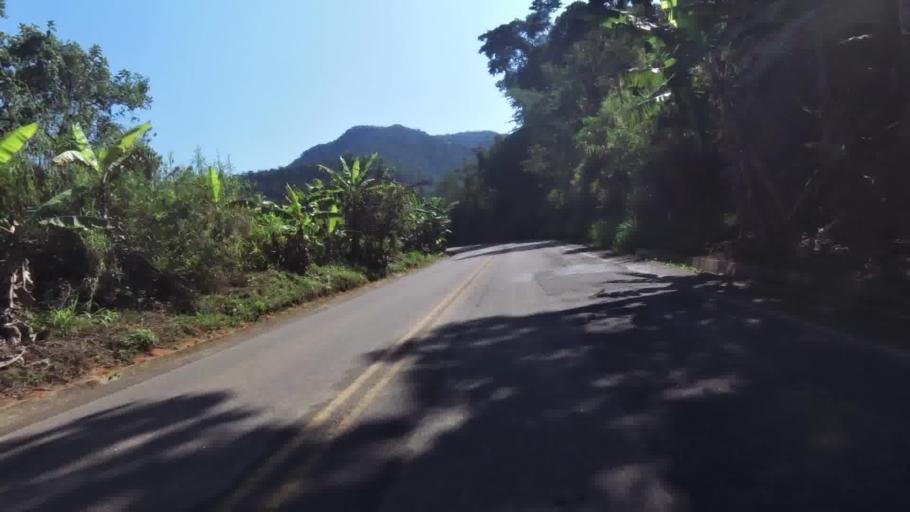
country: BR
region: Espirito Santo
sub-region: Alfredo Chaves
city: Alfredo Chaves
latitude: -20.6199
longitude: -40.7788
